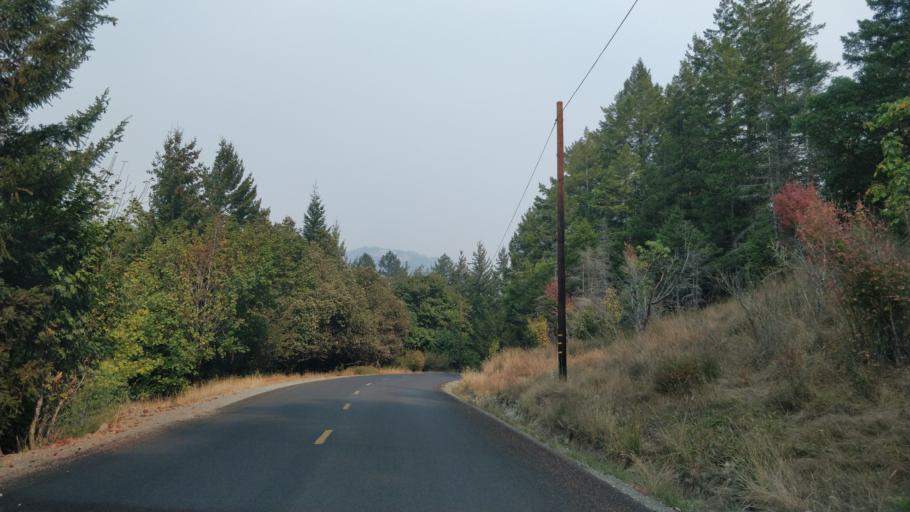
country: US
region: California
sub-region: Humboldt County
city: Rio Dell
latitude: 40.2520
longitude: -124.1850
